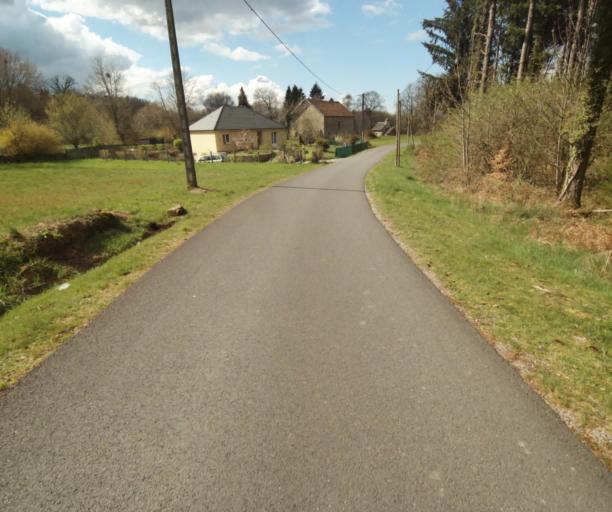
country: FR
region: Limousin
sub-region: Departement de la Correze
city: Correze
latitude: 45.2746
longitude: 1.8968
